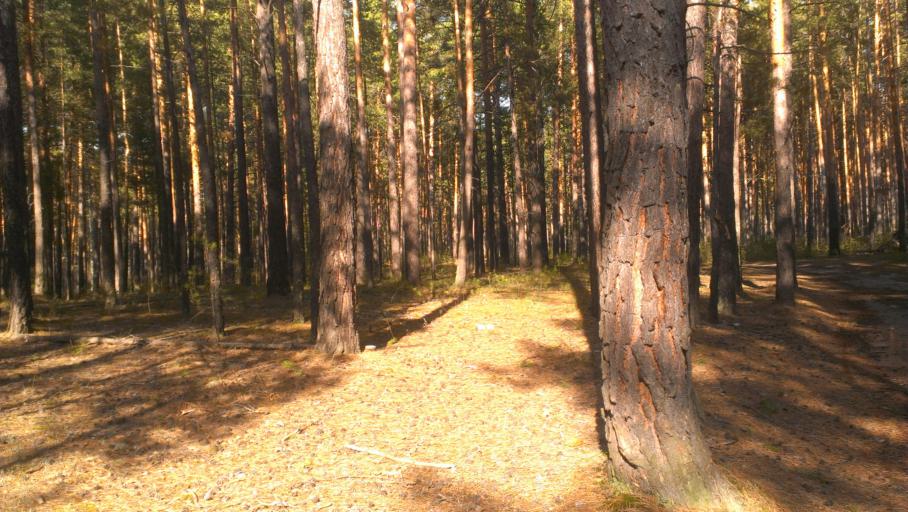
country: RU
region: Altai Krai
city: Yuzhnyy
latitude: 53.2822
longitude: 83.6981
